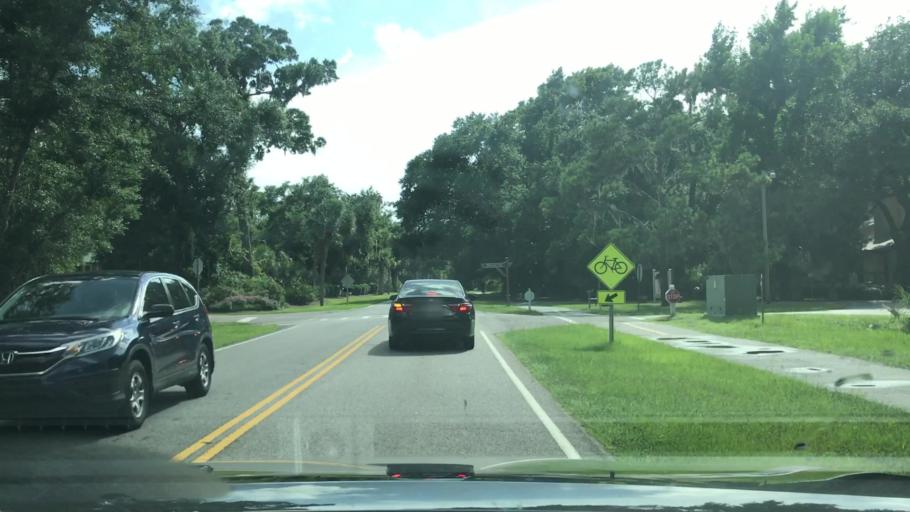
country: US
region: South Carolina
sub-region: Beaufort County
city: Hilton Head Island
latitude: 32.1456
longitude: -80.7597
